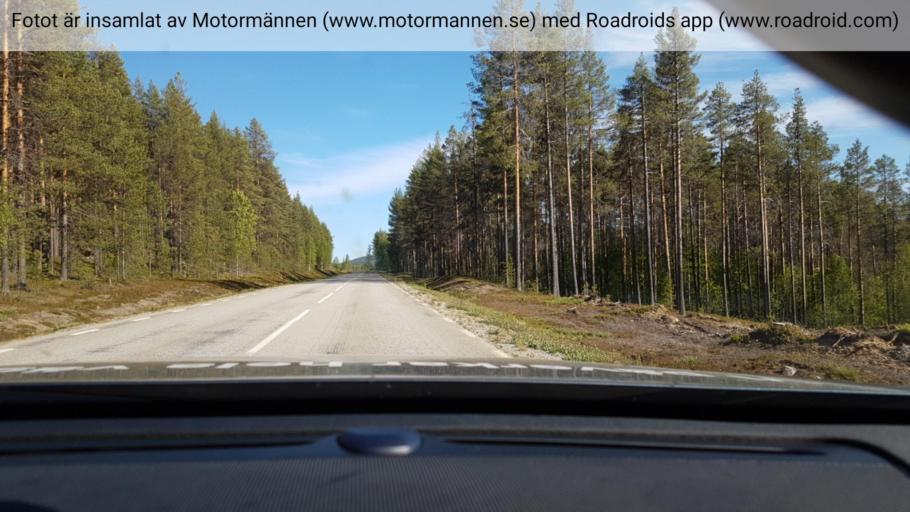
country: SE
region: Vaesterbotten
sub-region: Lycksele Kommun
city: Lycksele
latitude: 64.7832
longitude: 18.9942
